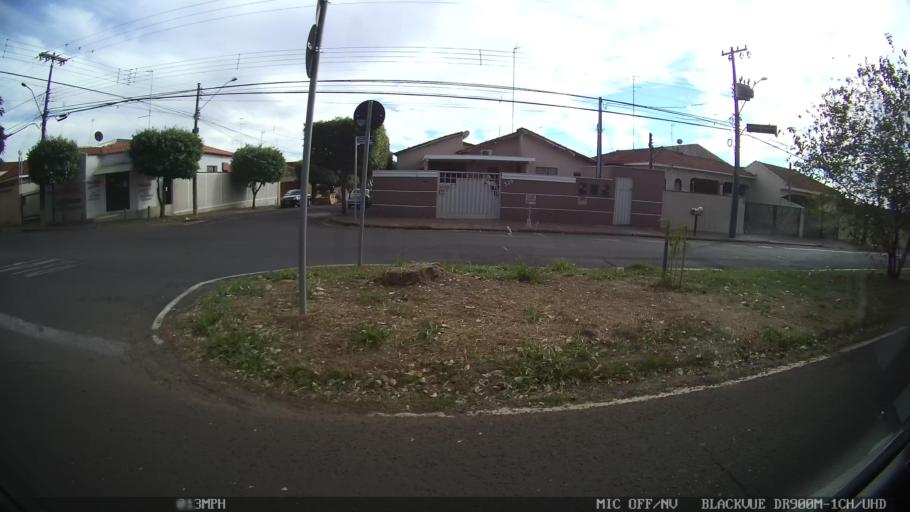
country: BR
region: Sao Paulo
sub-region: Catanduva
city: Catanduva
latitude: -21.1372
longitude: -48.9916
